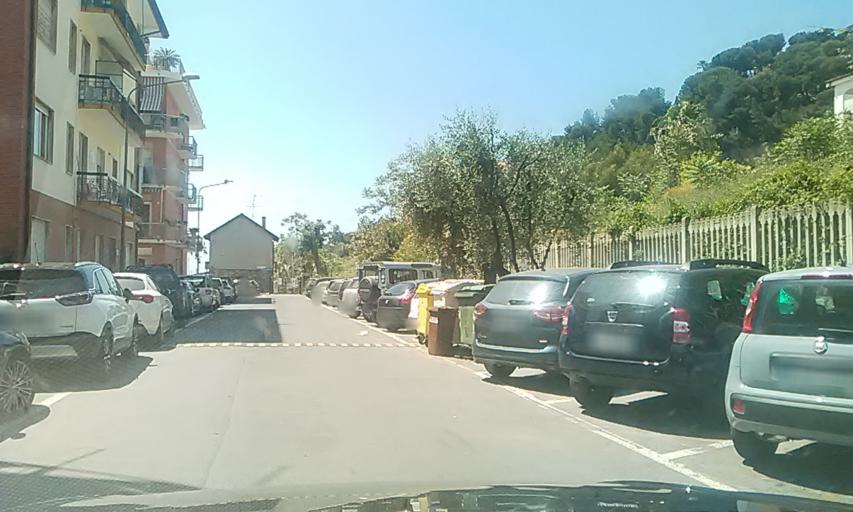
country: IT
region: Liguria
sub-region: Provincia di Savona
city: Andora
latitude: 43.9471
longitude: 8.1392
